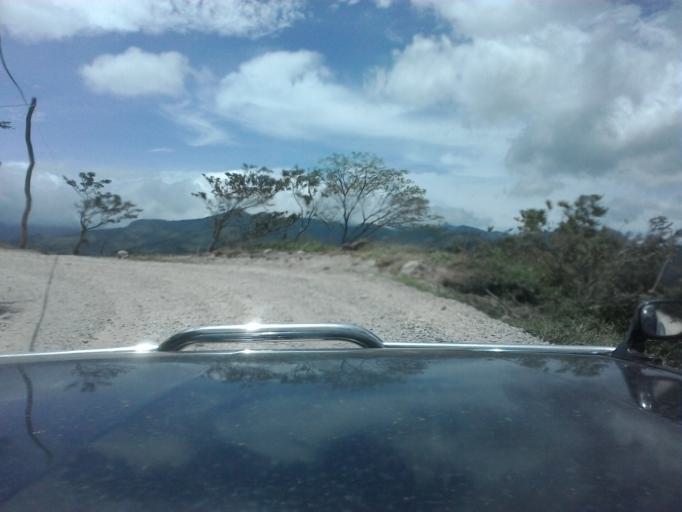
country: CR
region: Guanacaste
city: Juntas
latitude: 10.2470
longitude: -84.8401
